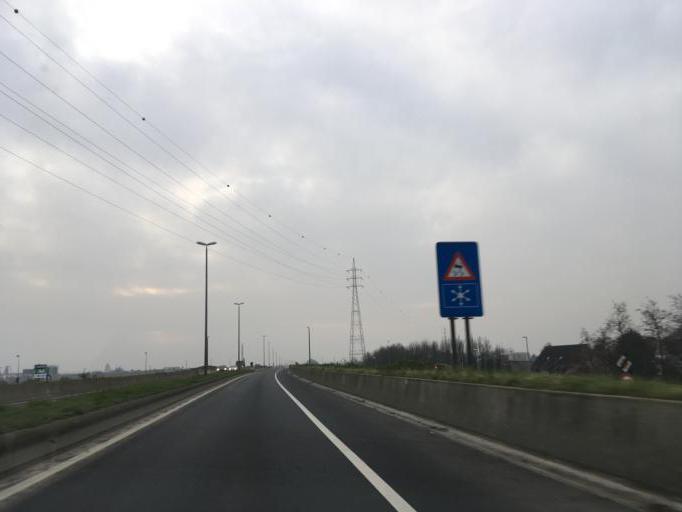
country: BE
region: Flanders
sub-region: Provincie West-Vlaanderen
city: Wielsbeke
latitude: 50.8993
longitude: 3.3970
